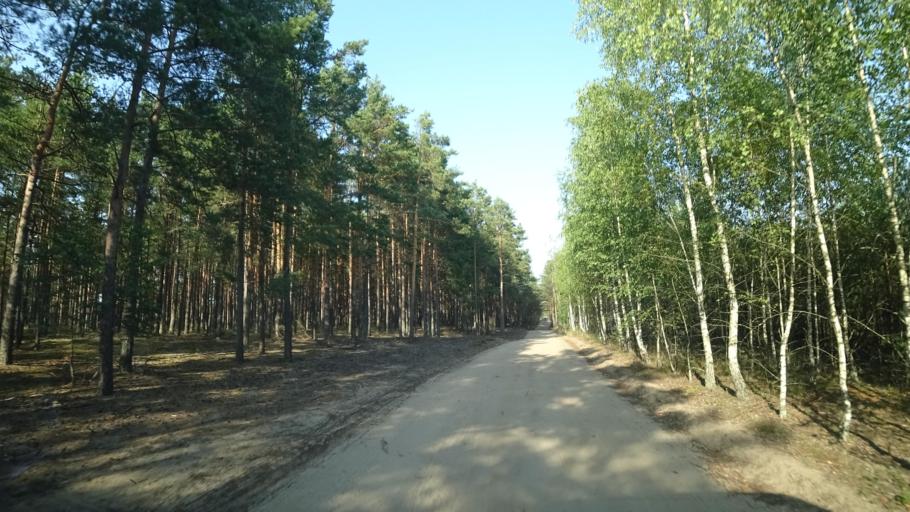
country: PL
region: Pomeranian Voivodeship
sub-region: Powiat chojnicki
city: Chojnice
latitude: 53.8658
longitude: 17.5286
